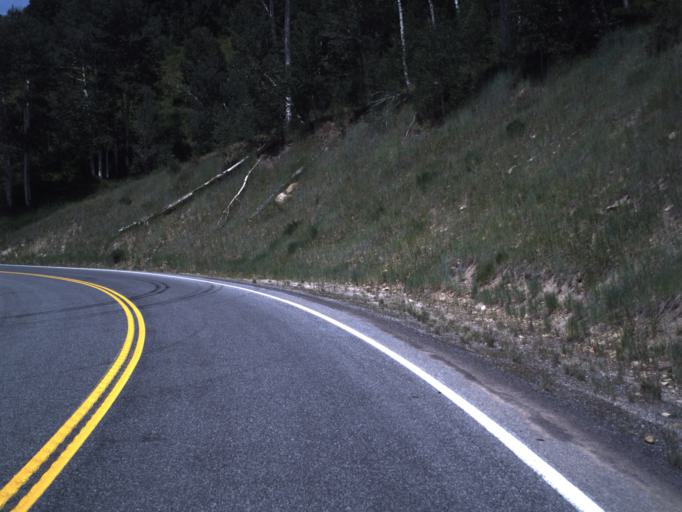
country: US
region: Utah
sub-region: Sanpete County
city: Fairview
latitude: 39.6831
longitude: -111.2308
